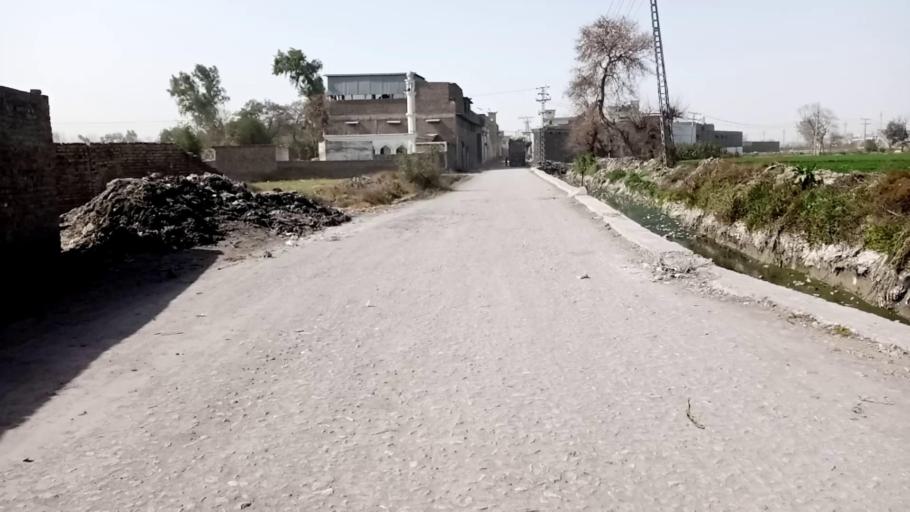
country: PK
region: Khyber Pakhtunkhwa
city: Peshawar
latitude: 34.0175
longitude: 71.6412
